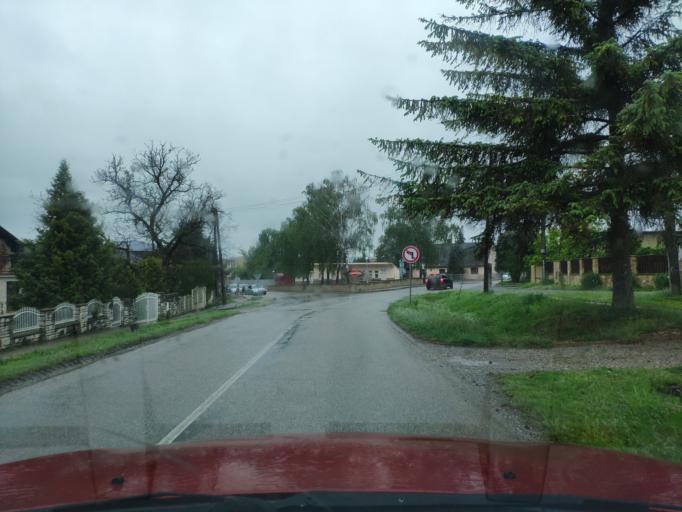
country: SK
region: Kosicky
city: Kosice
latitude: 48.7361
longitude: 21.4391
